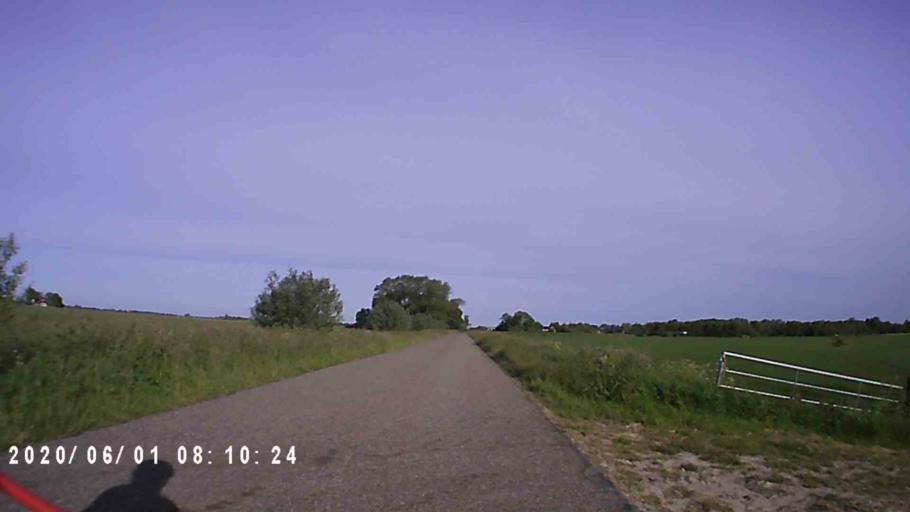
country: NL
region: Friesland
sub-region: Gemeente Ferwerderadiel
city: Burdaard
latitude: 53.2865
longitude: 5.8880
